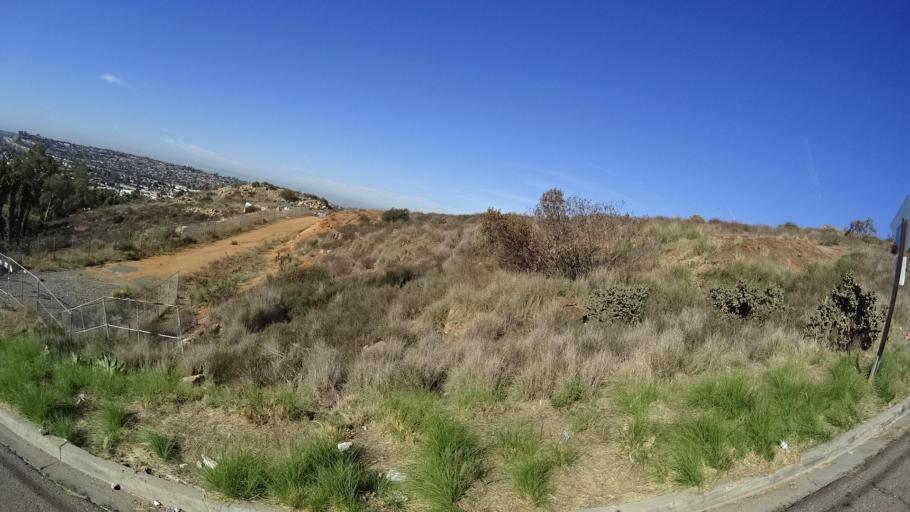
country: US
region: California
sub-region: San Diego County
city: La Presa
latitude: 32.7206
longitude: -116.9971
